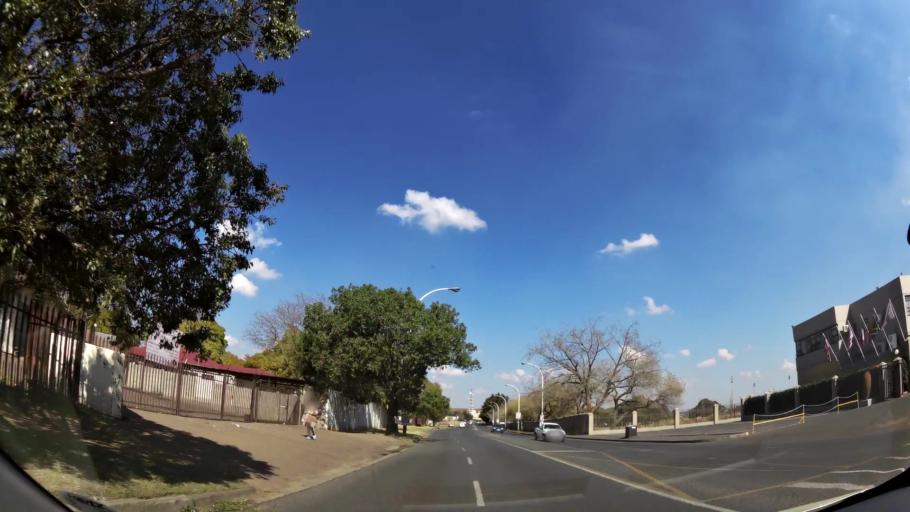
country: ZA
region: Mpumalanga
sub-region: Nkangala District Municipality
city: Witbank
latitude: -25.8808
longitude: 29.2196
